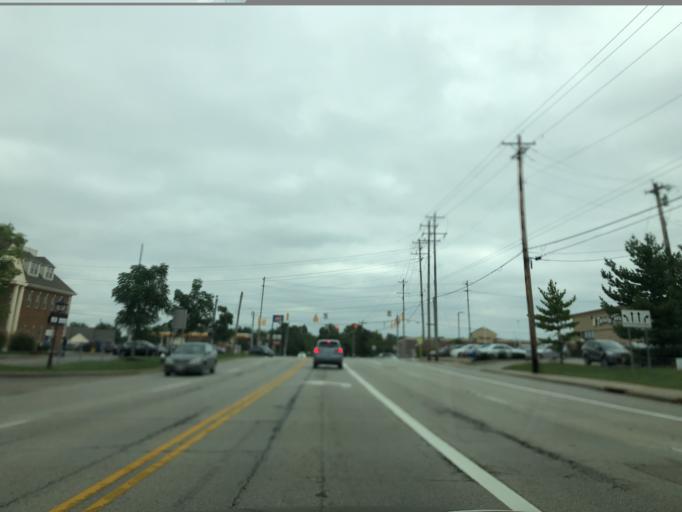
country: US
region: Ohio
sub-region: Hamilton County
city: Sixteen Mile Stand
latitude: 39.2733
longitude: -84.3283
